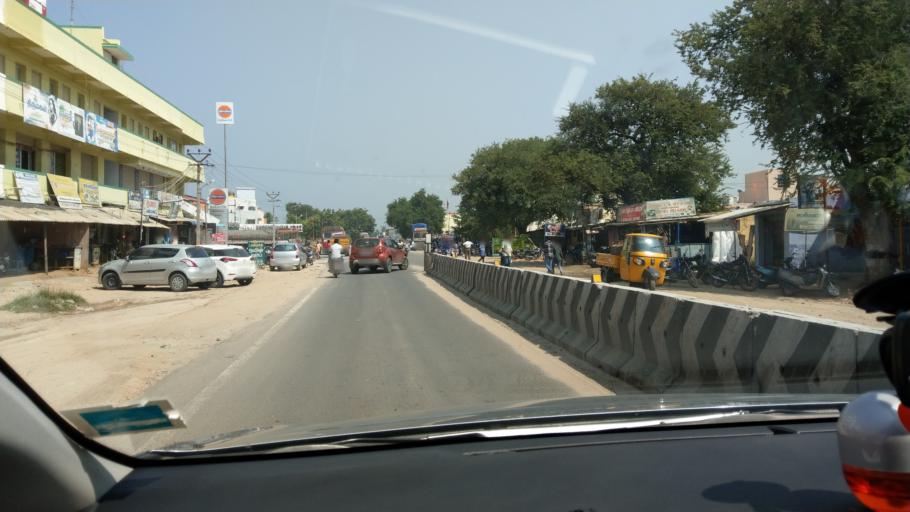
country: IN
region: Tamil Nadu
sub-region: Namakkal
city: Tiruchengode
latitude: 11.4793
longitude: 77.8811
